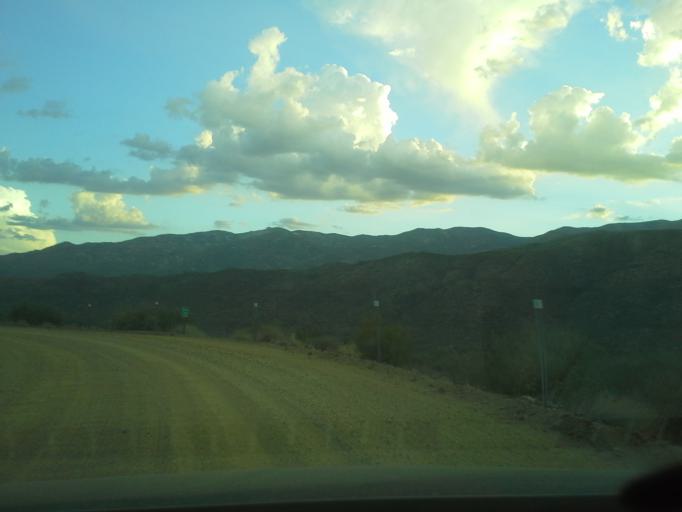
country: US
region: Arizona
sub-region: Yavapai County
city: Black Canyon City
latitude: 34.1772
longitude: -112.1652
